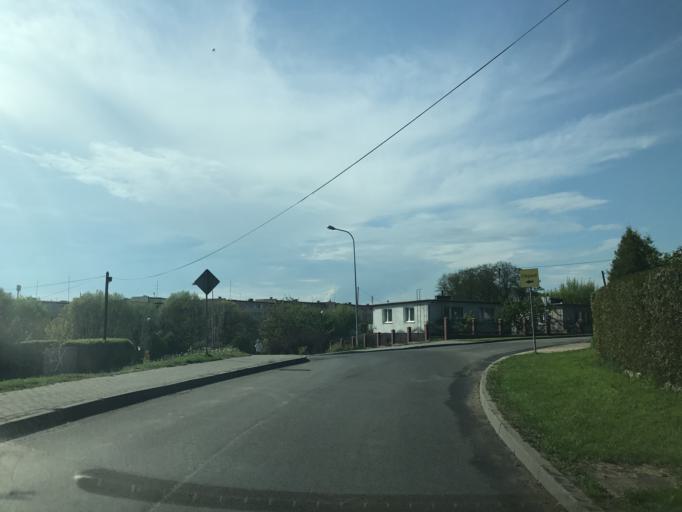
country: PL
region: Kujawsko-Pomorskie
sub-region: Powiat swiecki
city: Swiecie
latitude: 53.4106
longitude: 18.4334
